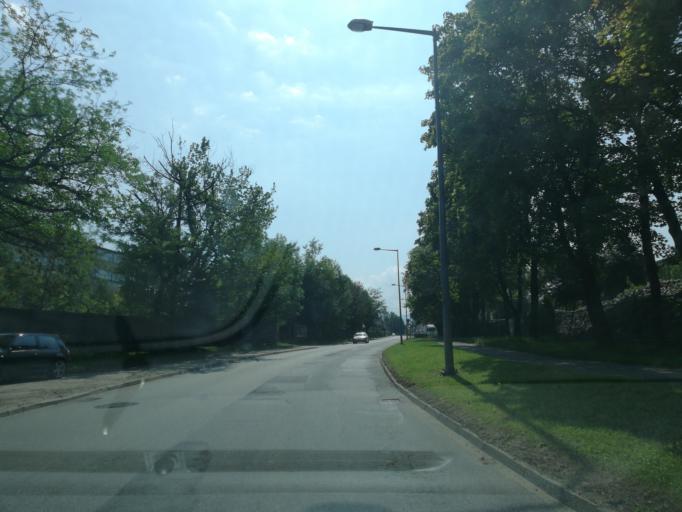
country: PL
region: Lesser Poland Voivodeship
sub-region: Powiat nowosadecki
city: Nowy Sacz
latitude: 49.6028
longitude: 20.7018
